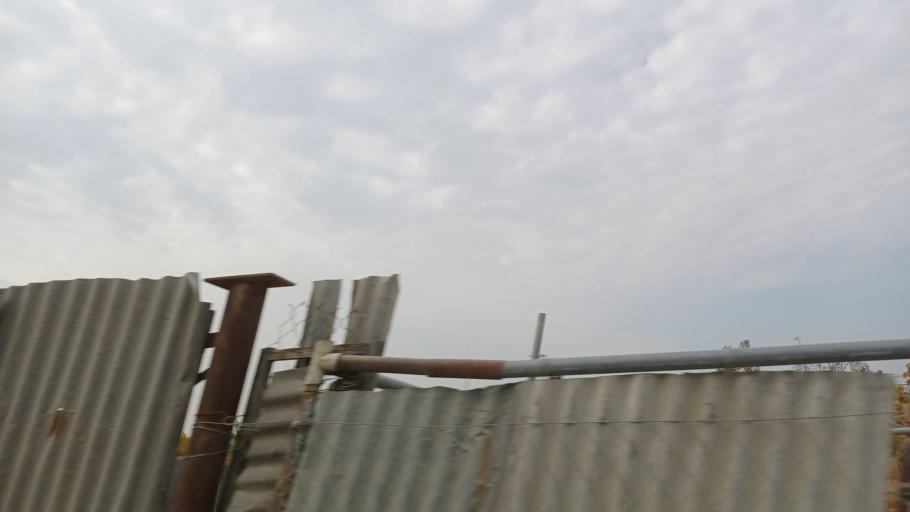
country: CY
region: Larnaka
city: Kolossi
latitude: 34.6668
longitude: 32.9503
